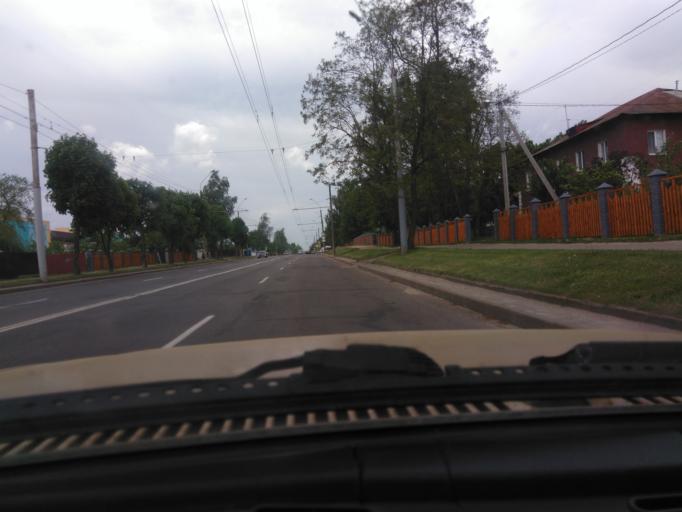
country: BY
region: Mogilev
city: Mahilyow
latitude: 53.9306
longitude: 30.3376
